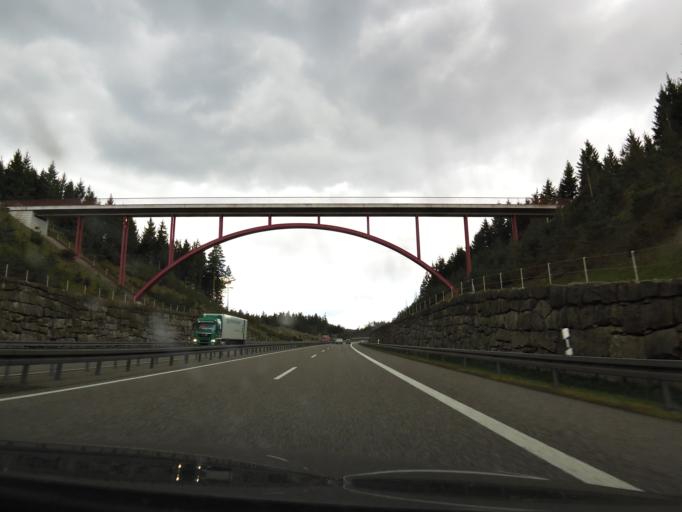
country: DE
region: Thuringia
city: Sankt Kilian
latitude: 50.5347
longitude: 10.7419
